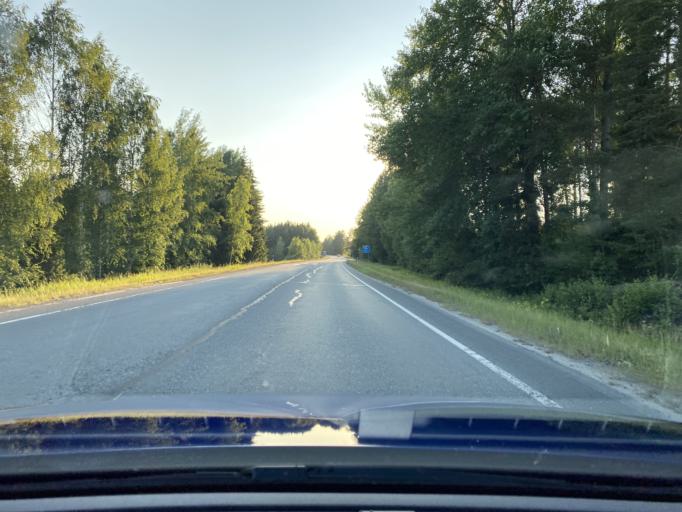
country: FI
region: Haeme
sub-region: Forssa
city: Tammela
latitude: 60.8274
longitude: 23.7383
